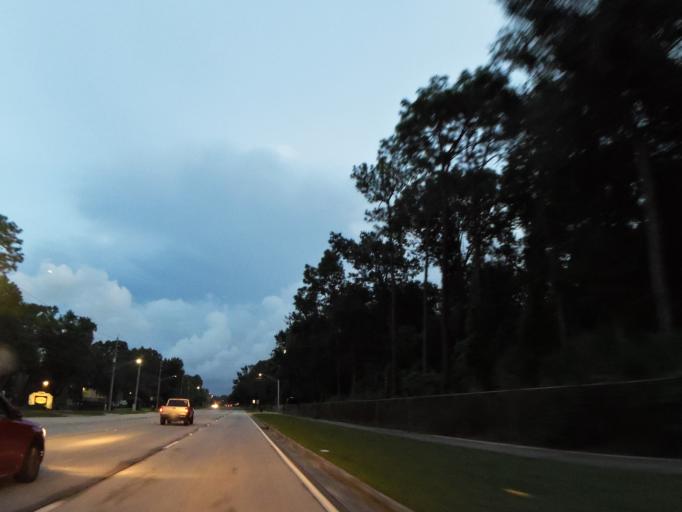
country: US
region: Florida
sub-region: Duval County
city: Jacksonville
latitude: 30.3598
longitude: -81.6055
